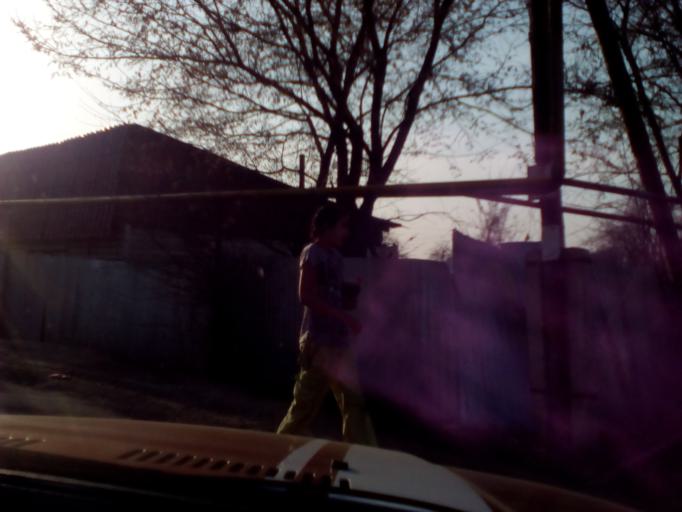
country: KZ
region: Almaty Oblysy
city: Burunday
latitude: 43.1596
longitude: 76.4199
